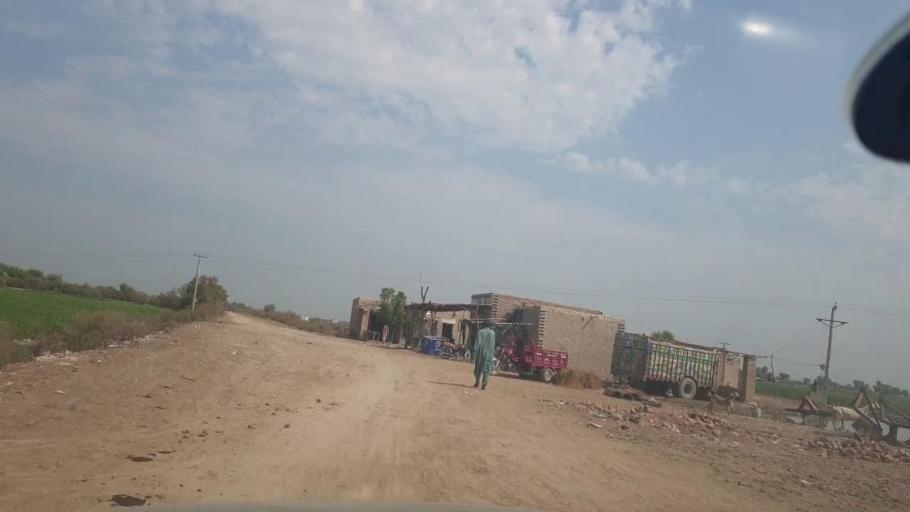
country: PK
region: Balochistan
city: Mehrabpur
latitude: 28.1055
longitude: 68.0915
